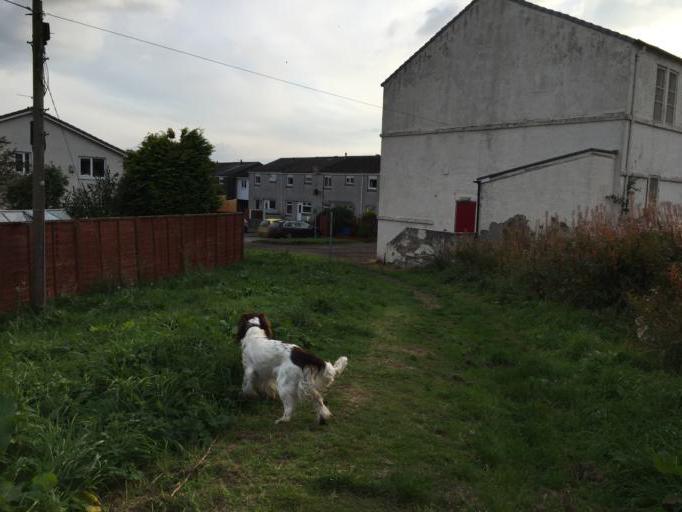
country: GB
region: Scotland
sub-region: West Lothian
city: Livingston
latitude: 55.9326
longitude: -3.5088
